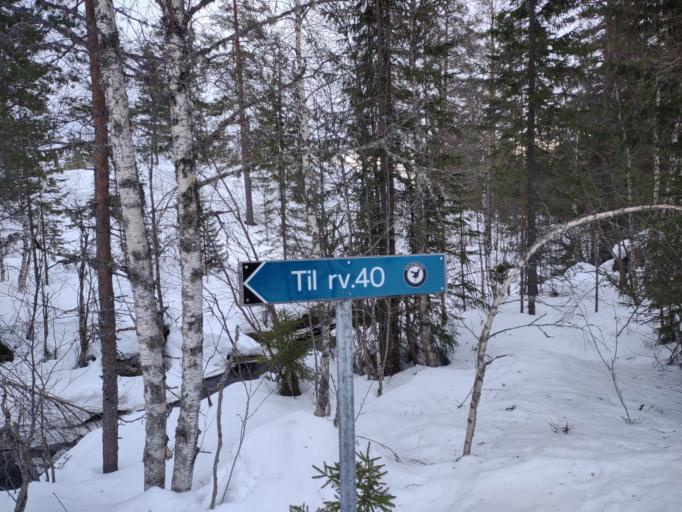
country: NO
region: Buskerud
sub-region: Flesberg
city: Lampeland
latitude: 59.7385
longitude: 9.5157
